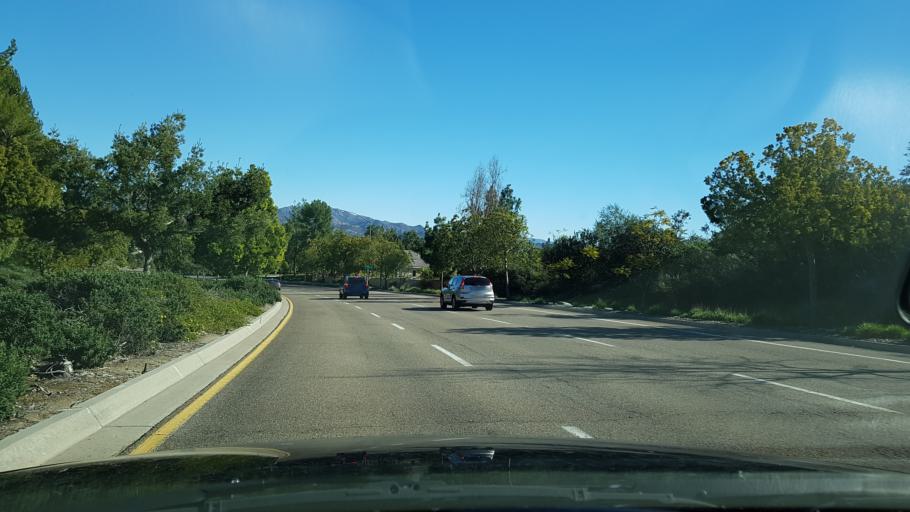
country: US
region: California
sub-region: San Diego County
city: Poway
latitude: 32.9711
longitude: -117.0734
